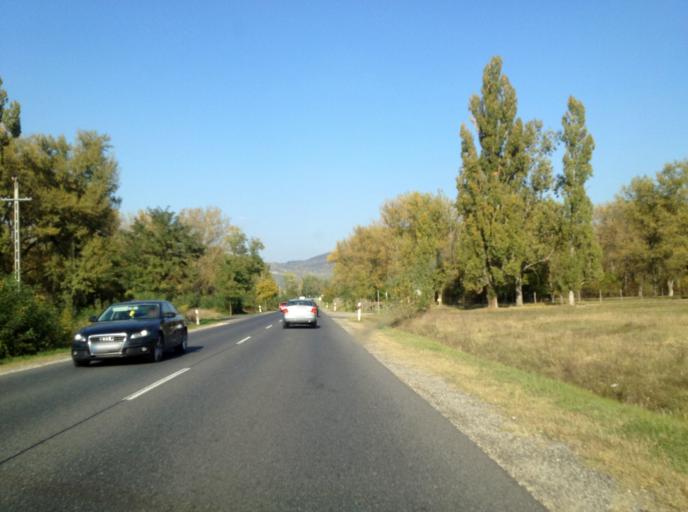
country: HU
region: Komarom-Esztergom
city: Dorog
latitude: 47.7564
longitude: 18.7416
